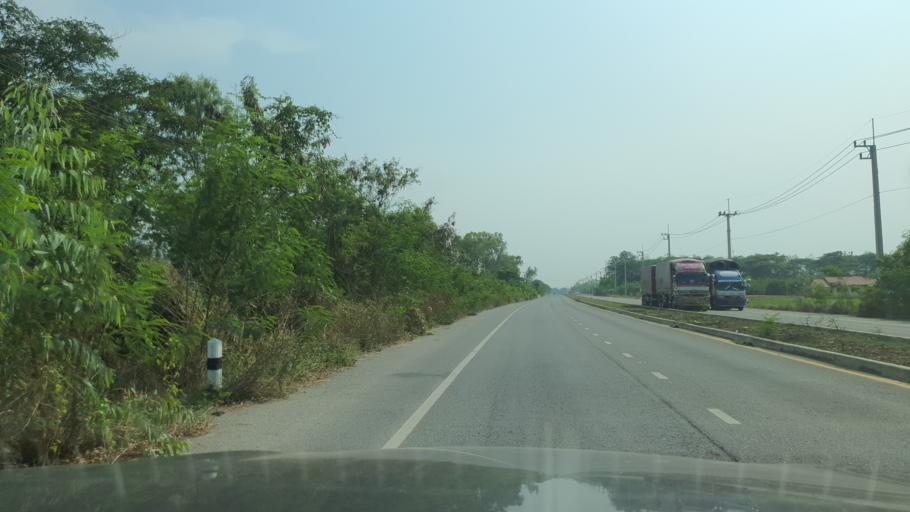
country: TH
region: Lamphun
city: Lamphun
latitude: 18.5992
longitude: 99.0063
